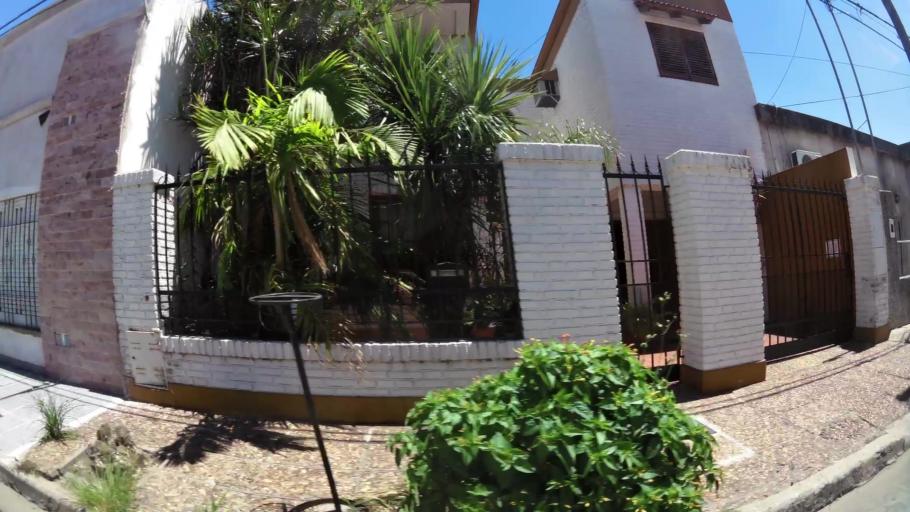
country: AR
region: Santa Fe
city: Santa Fe de la Vera Cruz
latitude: -31.6511
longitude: -60.7209
